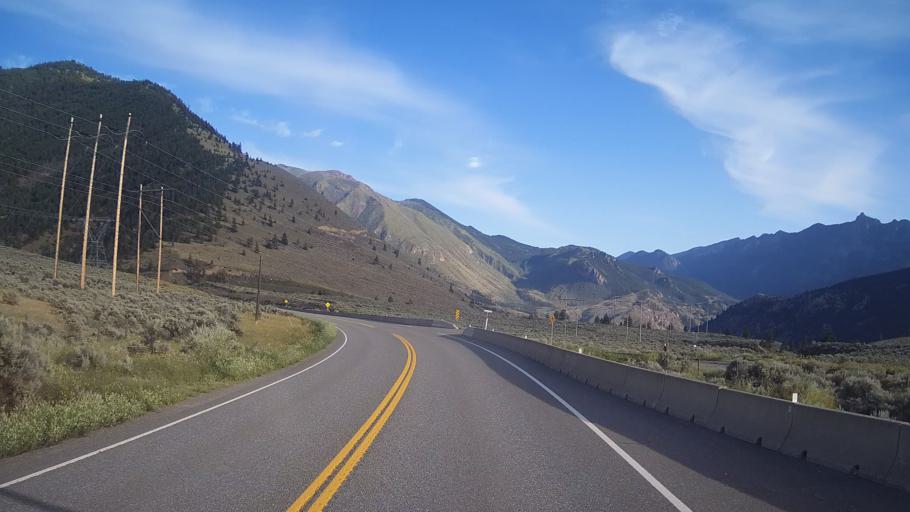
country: CA
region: British Columbia
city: Lillooet
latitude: 50.7988
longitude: -121.8440
